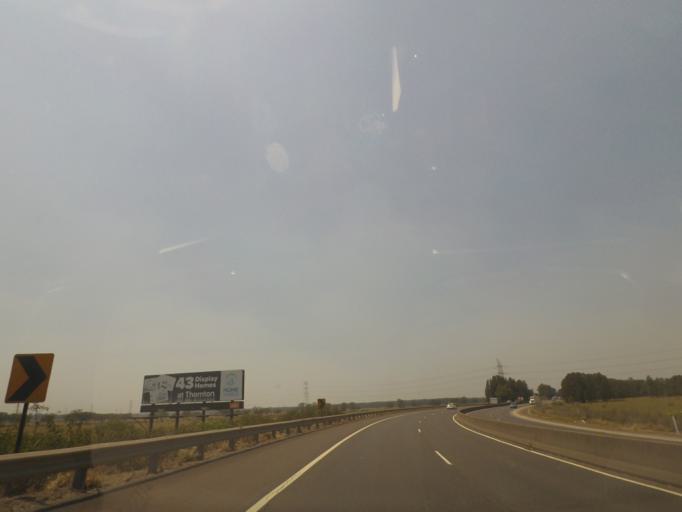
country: AU
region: New South Wales
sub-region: Newcastle
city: Beresfield
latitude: -32.8105
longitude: 151.6741
